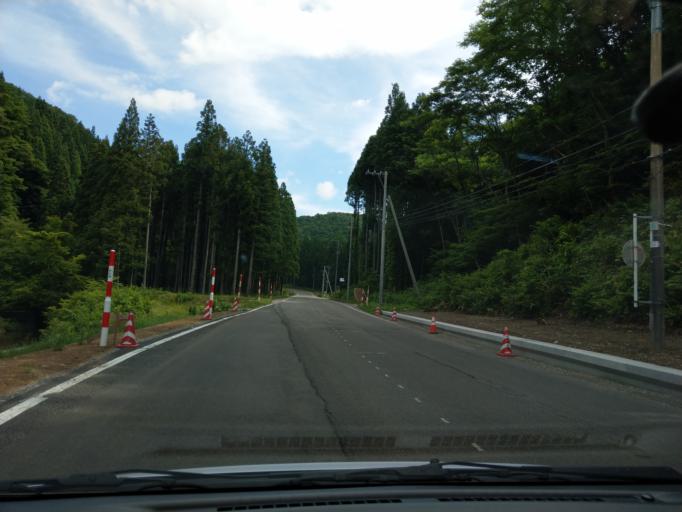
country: JP
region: Akita
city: Kakunodatemachi
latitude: 39.7086
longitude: 140.5868
